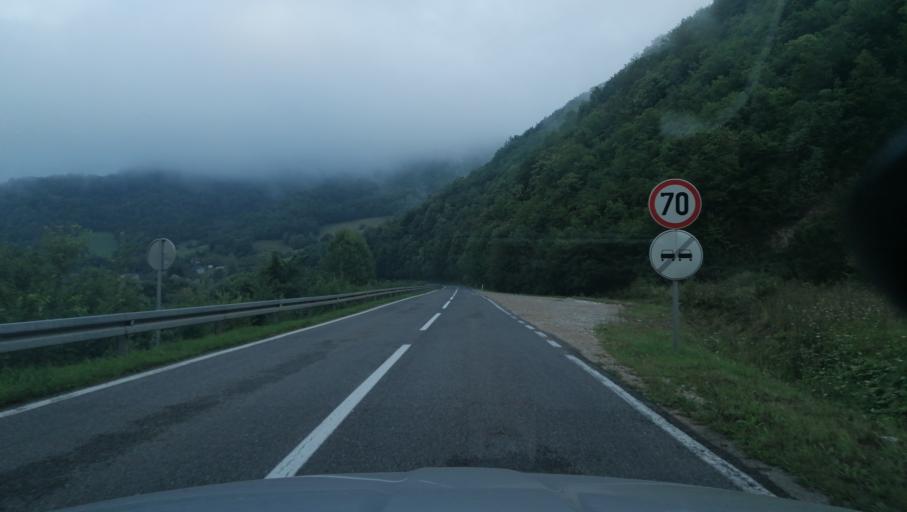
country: BA
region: Federation of Bosnia and Herzegovina
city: Donji Vakuf
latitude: 44.1880
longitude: 17.3428
